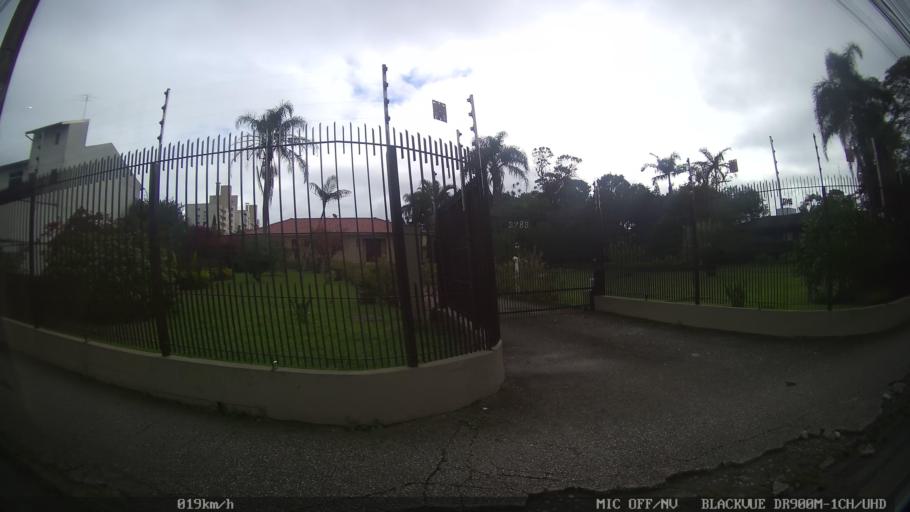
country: BR
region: Santa Catarina
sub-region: Sao Jose
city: Campinas
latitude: -27.5830
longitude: -48.6168
